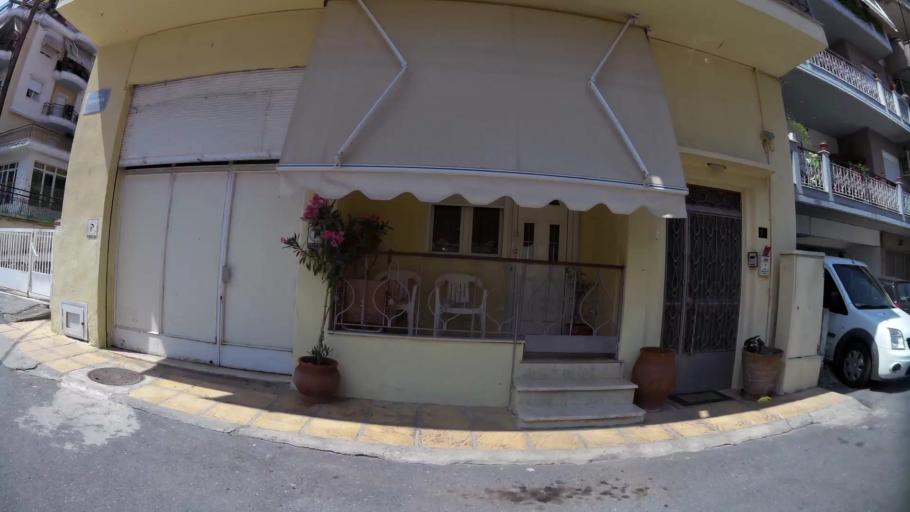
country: GR
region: Central Macedonia
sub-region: Nomos Imathias
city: Veroia
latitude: 40.5129
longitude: 22.2078
